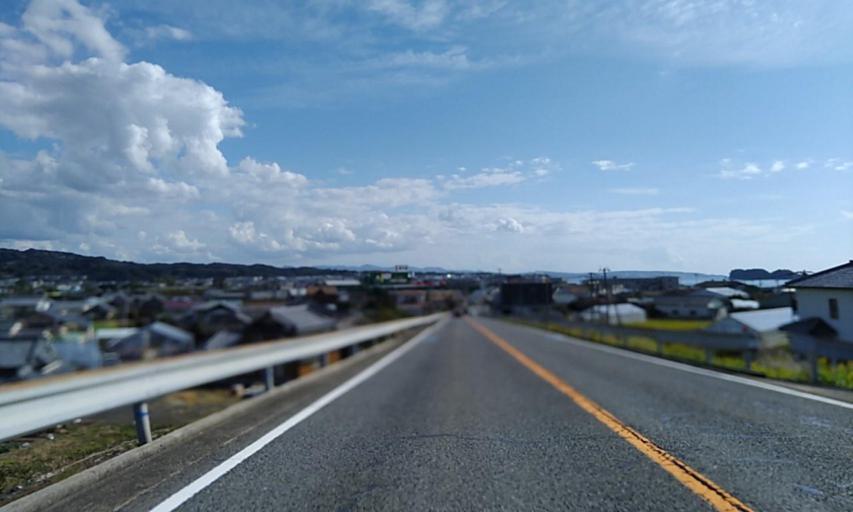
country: JP
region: Wakayama
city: Tanabe
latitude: 33.7753
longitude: 135.3116
